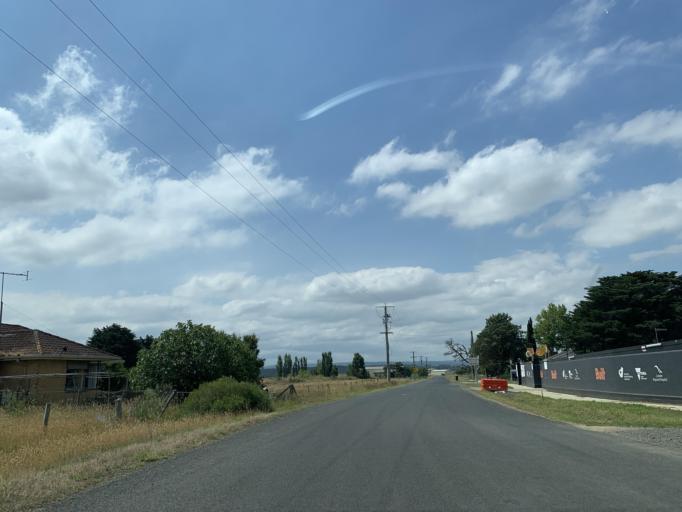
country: AU
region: Victoria
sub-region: Latrobe
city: Morwell
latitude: -38.2177
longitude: 146.4688
